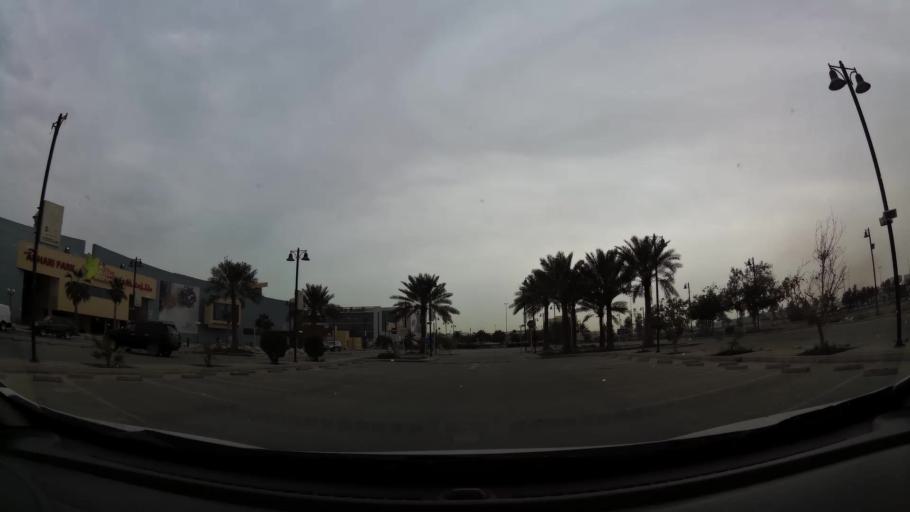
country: BH
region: Manama
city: Jidd Hafs
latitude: 26.1979
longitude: 50.5432
